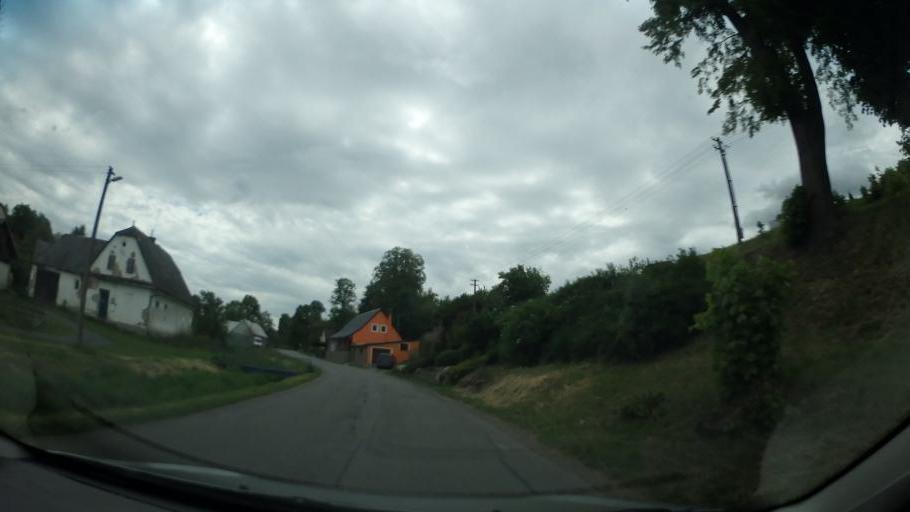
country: CZ
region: Pardubicky
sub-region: Okres Svitavy
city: Moravska Trebova
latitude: 49.8319
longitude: 16.7018
